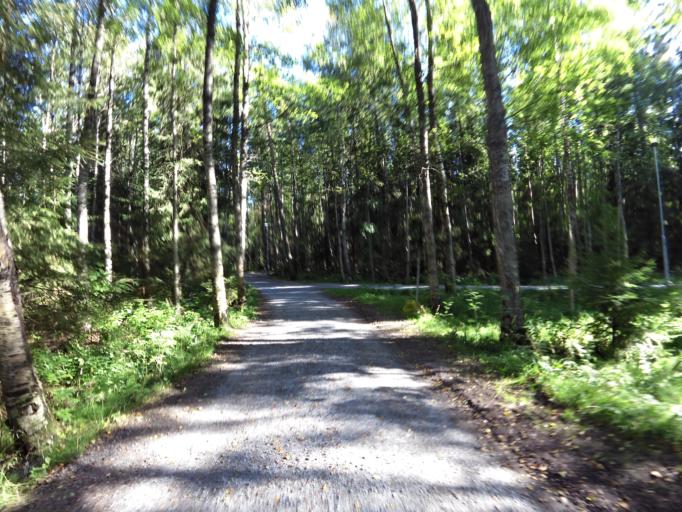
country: FI
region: Pirkanmaa
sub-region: Tampere
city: Pirkkala
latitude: 61.5070
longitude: 23.6108
